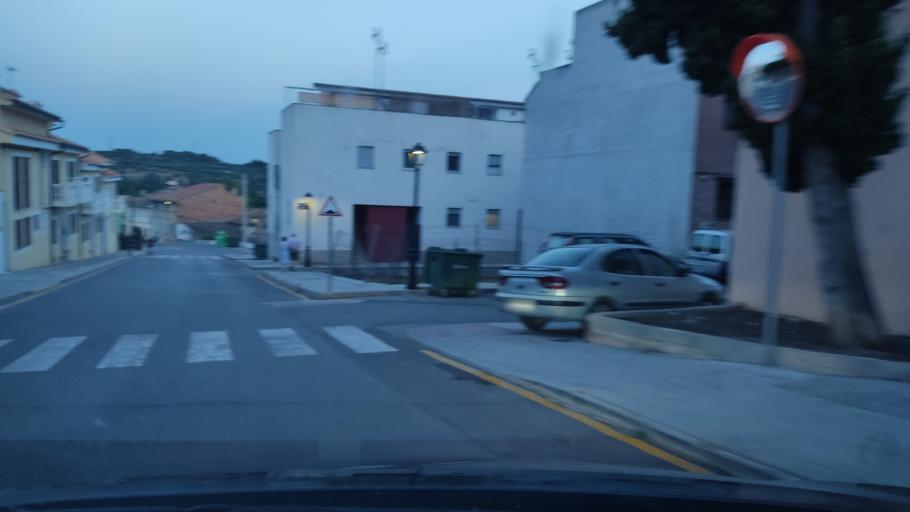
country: ES
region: Valencia
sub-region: Provincia de Castello
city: Jerica
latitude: 39.9102
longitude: -0.5704
